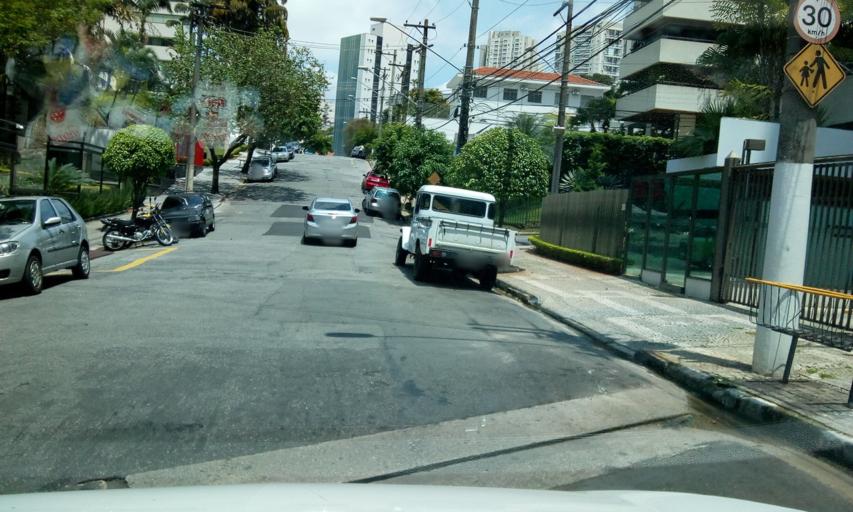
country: BR
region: Sao Paulo
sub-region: Sao Paulo
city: Sao Paulo
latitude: -23.5728
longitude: -46.6349
